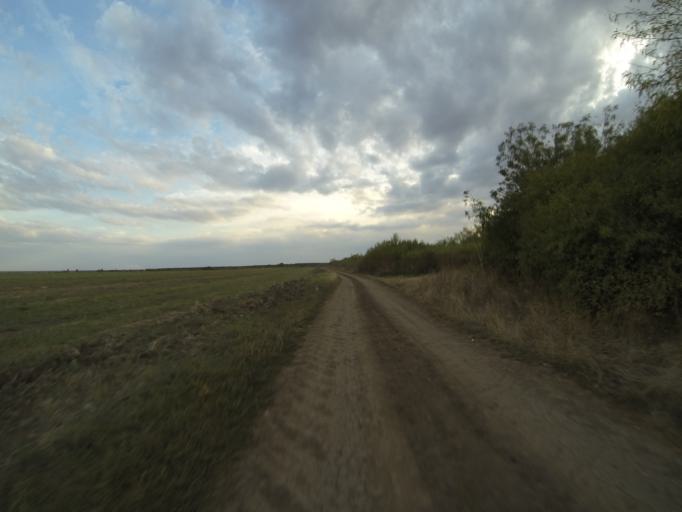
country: RO
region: Dolj
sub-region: Comuna Ceratu
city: Ceratu
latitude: 44.1002
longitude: 23.6913
